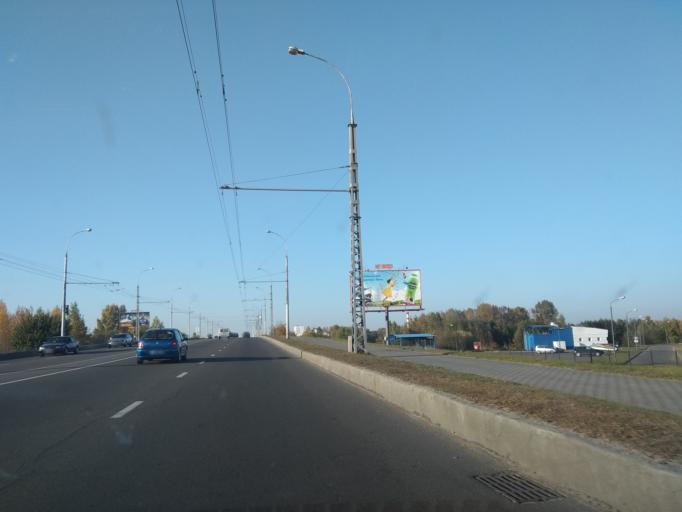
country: BY
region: Brest
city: Brest
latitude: 52.0838
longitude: 23.7365
